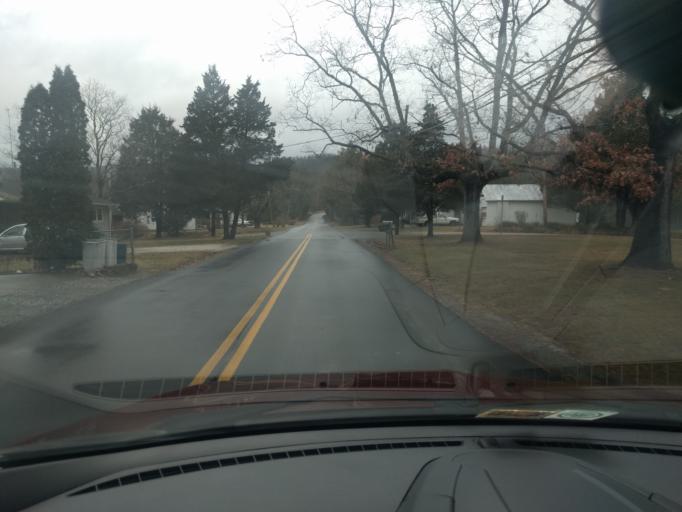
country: US
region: Virginia
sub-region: Botetourt County
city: Fincastle
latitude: 37.5465
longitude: -79.8759
